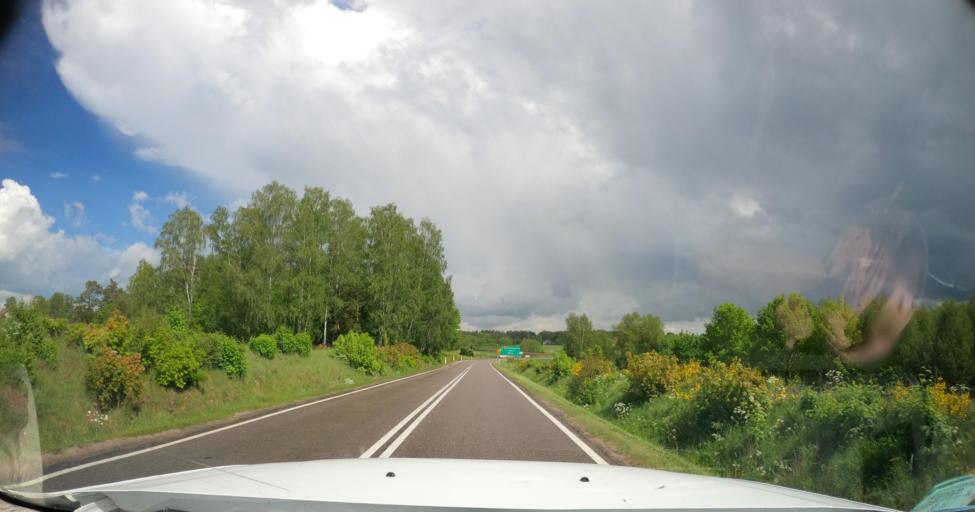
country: PL
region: Pomeranian Voivodeship
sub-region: Powiat leborski
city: Cewice
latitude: 54.3418
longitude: 17.6793
